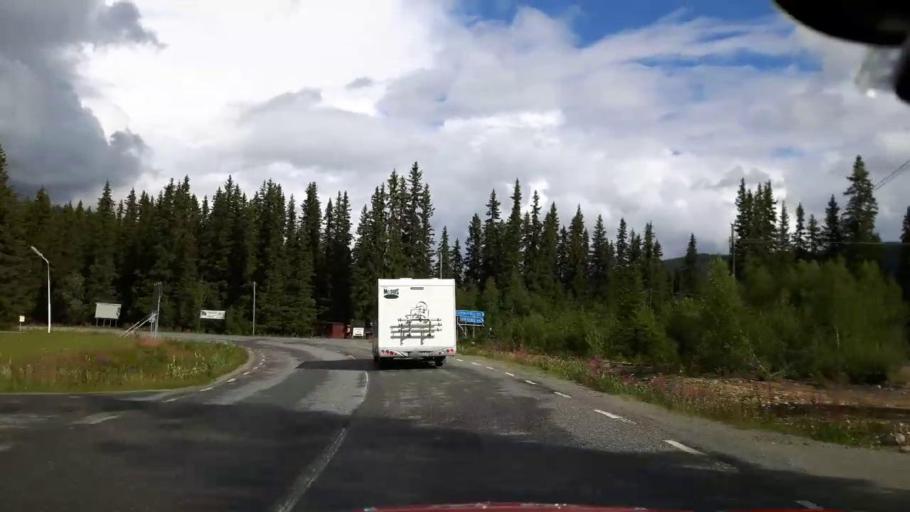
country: SE
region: Vaesterbotten
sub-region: Vilhelmina Kommun
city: Sjoberg
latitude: 64.9379
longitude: 15.8585
